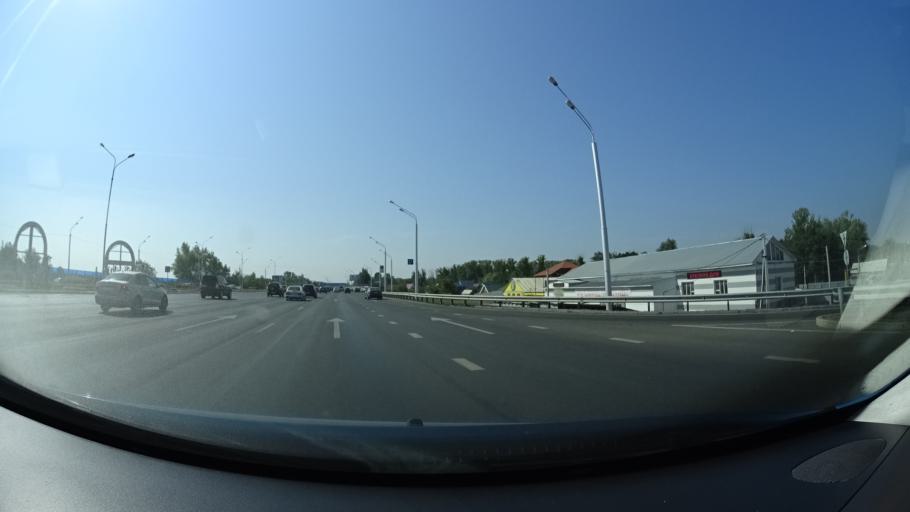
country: RU
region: Bashkortostan
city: Ufa
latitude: 54.7006
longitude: 55.9481
